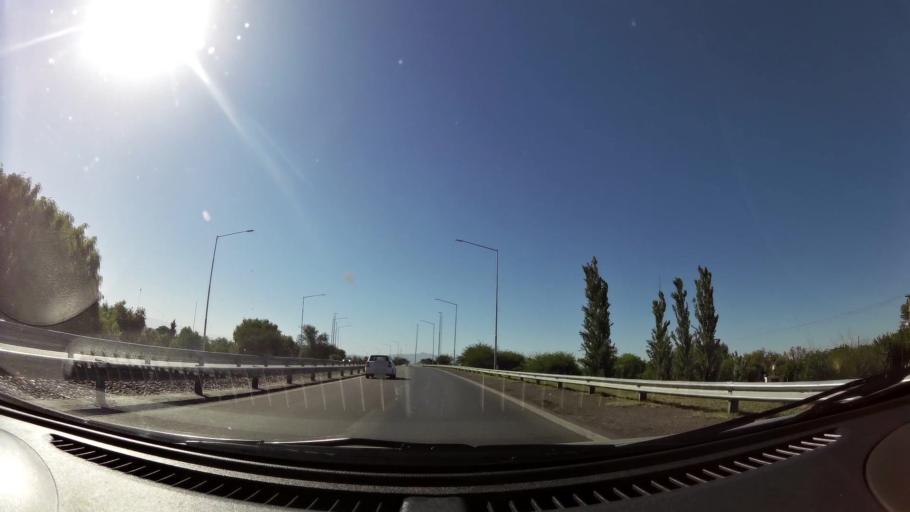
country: AR
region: San Juan
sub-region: Departamento de Santa Lucia
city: Santa Lucia
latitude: -31.5226
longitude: -68.5032
